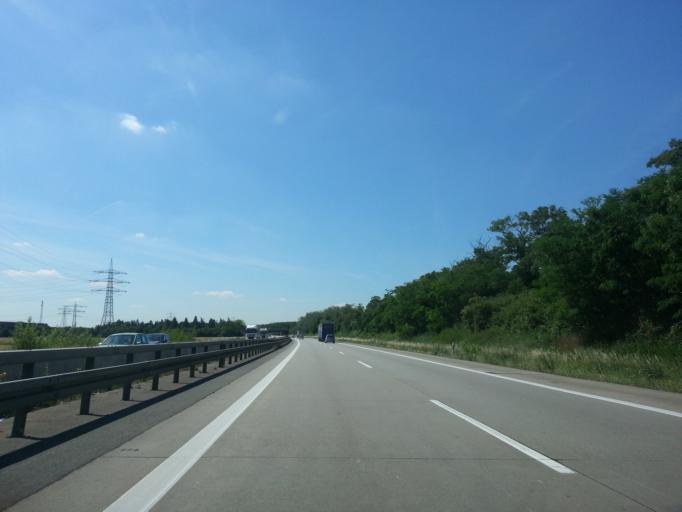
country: DE
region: Baden-Wuerttemberg
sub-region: Karlsruhe Region
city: Ilvesheim
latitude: 49.4414
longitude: 8.5403
